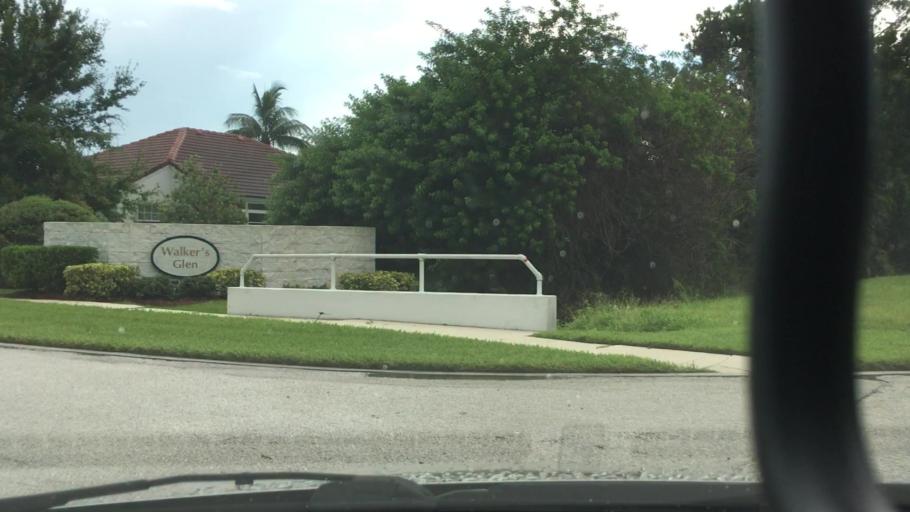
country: US
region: Florida
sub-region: Indian River County
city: Vero Beach South
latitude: 27.6460
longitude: -80.4330
